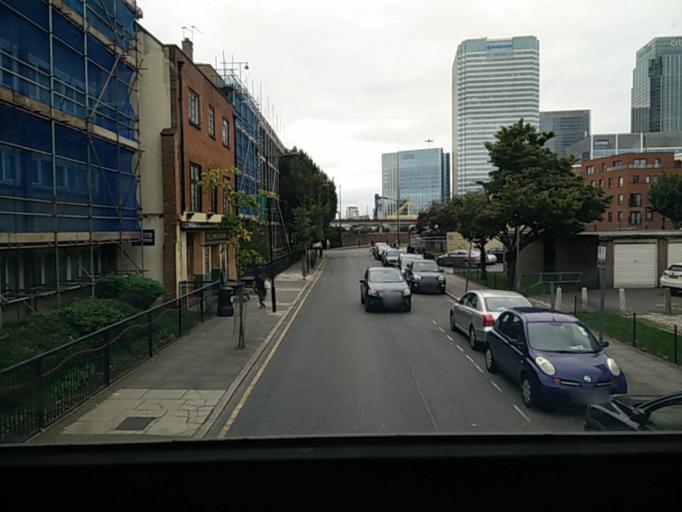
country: GB
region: England
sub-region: Greater London
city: Poplar
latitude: 51.5096
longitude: -0.0120
